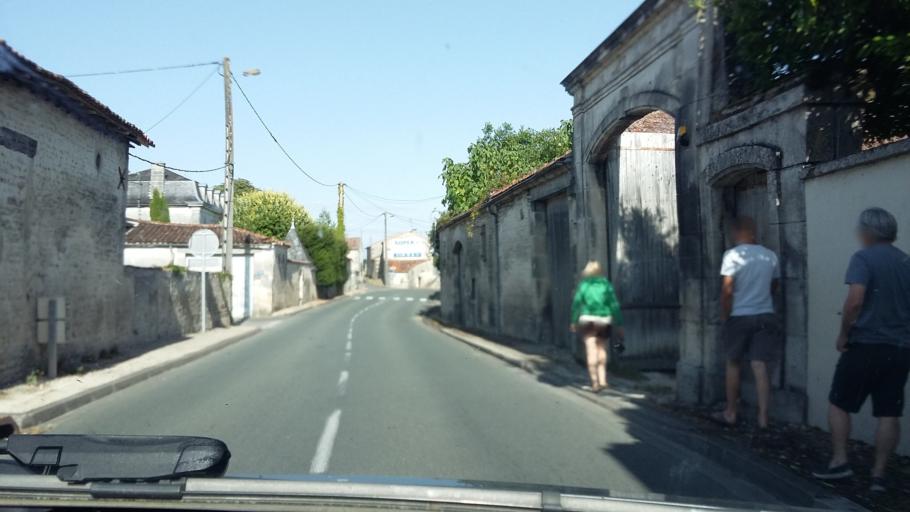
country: FR
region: Poitou-Charentes
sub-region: Departement de la Charente
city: Nercillac
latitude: 45.8293
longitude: -0.1921
